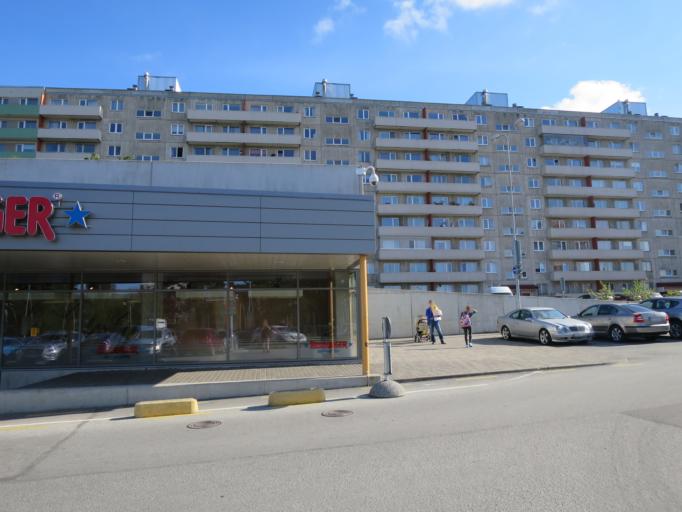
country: EE
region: Harju
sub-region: Tallinna linn
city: Tallinn
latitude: 59.4009
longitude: 24.6967
